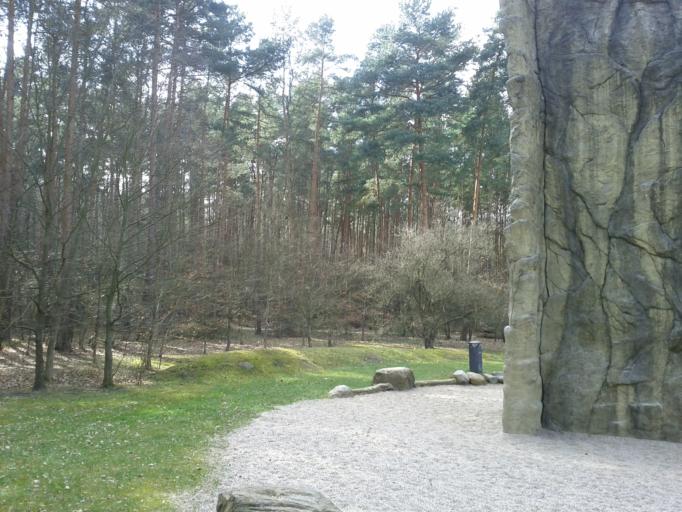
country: DE
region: Brandenburg
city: Potsdam
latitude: 52.3640
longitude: 13.0853
